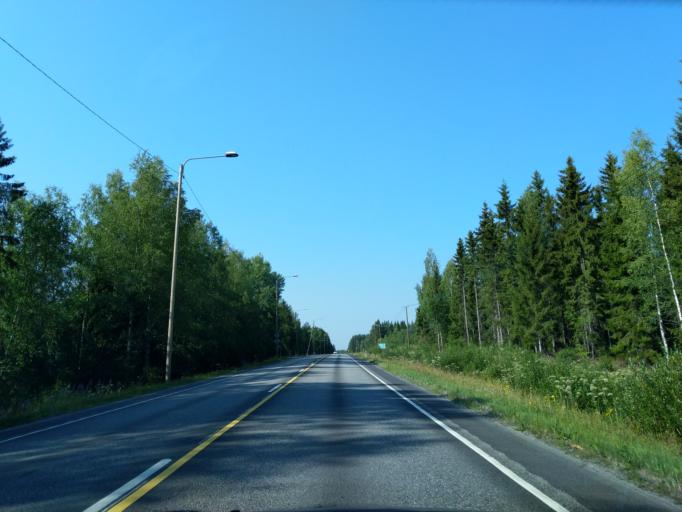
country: FI
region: Satakunta
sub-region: Pori
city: Pomarkku
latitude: 61.7082
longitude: 22.0297
